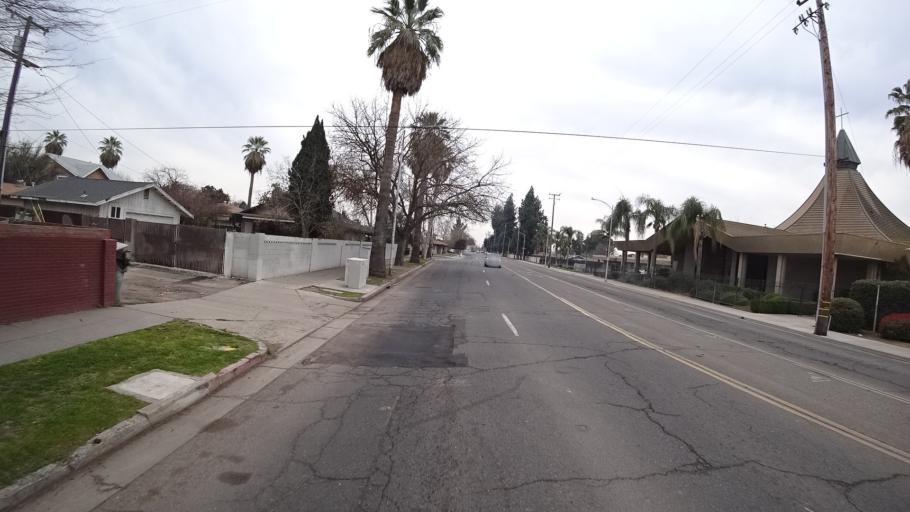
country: US
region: California
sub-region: Fresno County
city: Fresno
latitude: 36.7388
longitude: -119.7724
